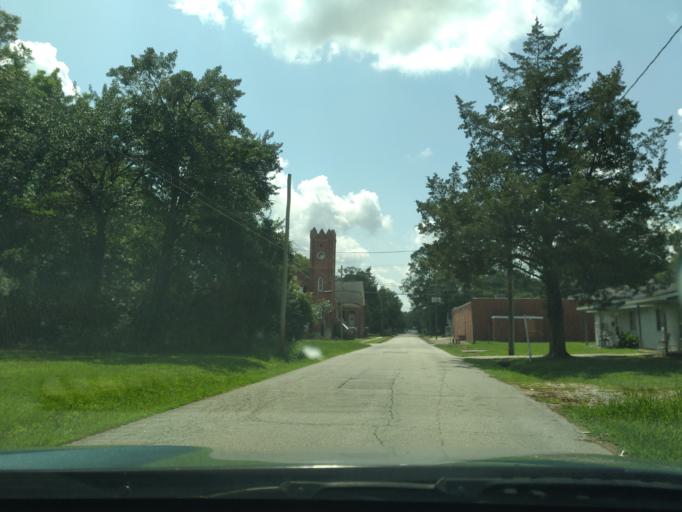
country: US
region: North Carolina
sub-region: Washington County
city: Plymouth
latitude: 35.8663
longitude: -76.7461
